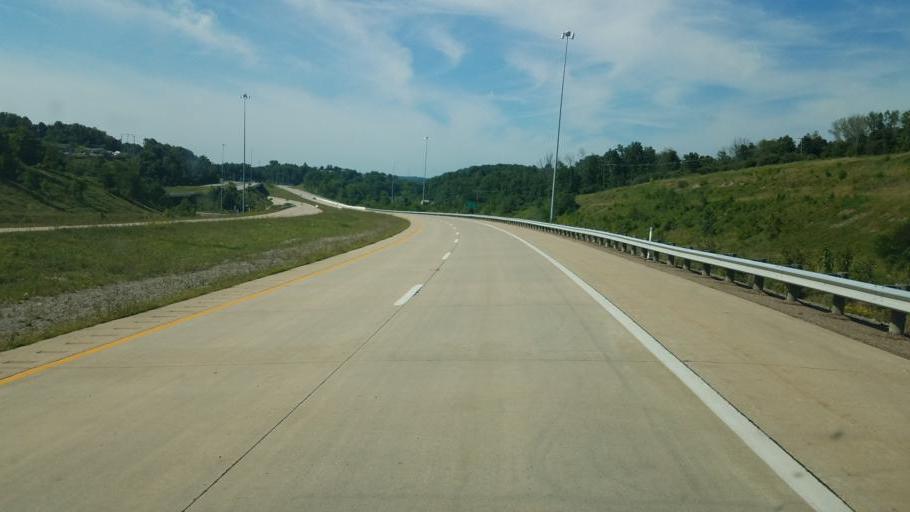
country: US
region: Ohio
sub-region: Athens County
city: Athens
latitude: 39.2996
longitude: -82.1023
